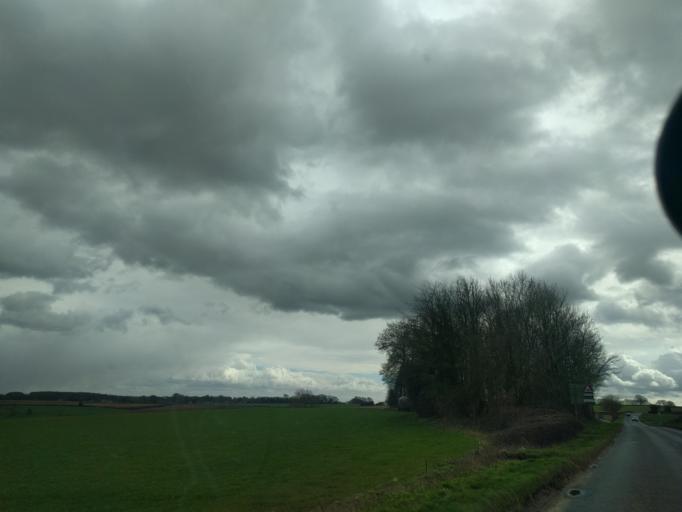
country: GB
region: England
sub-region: Gloucestershire
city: Nailsworth
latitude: 51.6771
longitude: -2.2767
